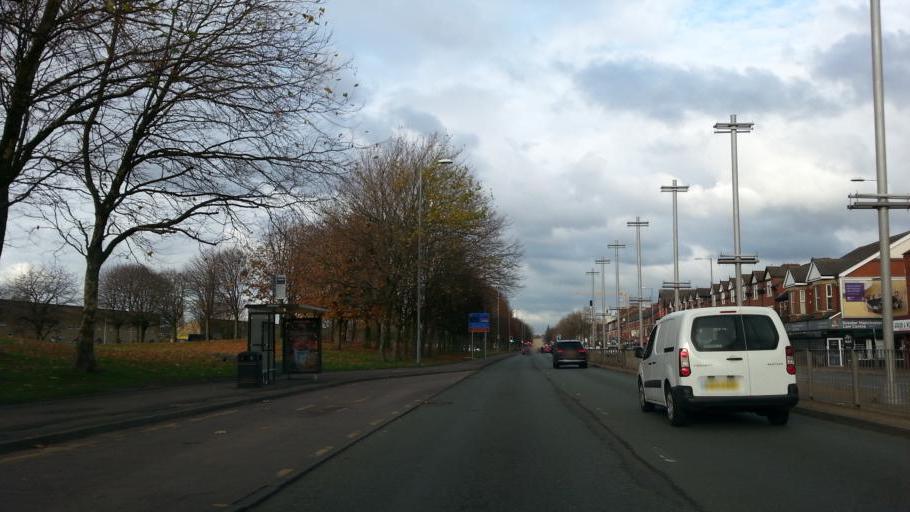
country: GB
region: England
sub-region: Manchester
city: Hulme
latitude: 53.4538
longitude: -2.2452
